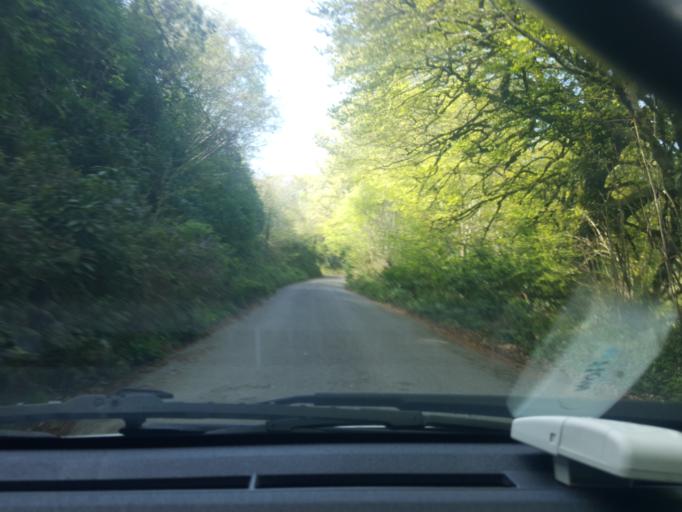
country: IE
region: Munster
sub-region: County Cork
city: Bandon
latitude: 51.7668
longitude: -8.6804
